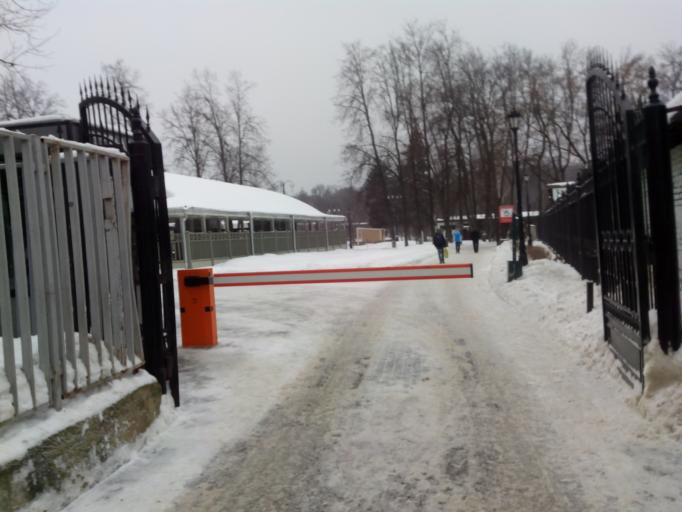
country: RU
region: Moscow
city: Ostankinskiy
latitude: 55.8289
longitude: 37.6190
